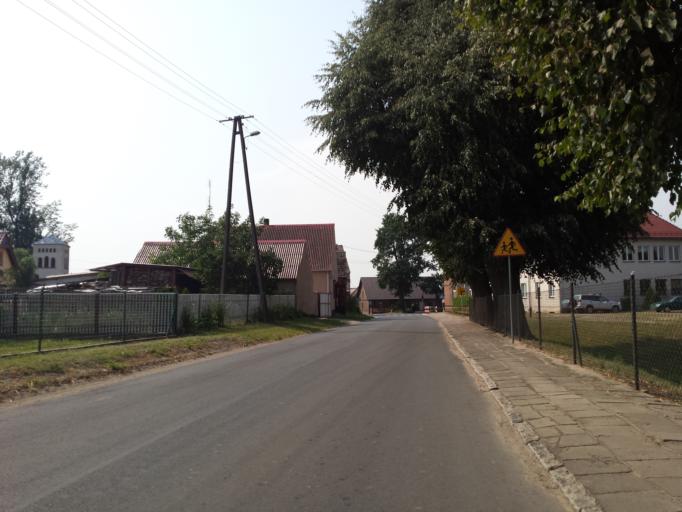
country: PL
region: Greater Poland Voivodeship
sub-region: Powiat czarnkowsko-trzcianecki
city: Polajewo
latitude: 52.7746
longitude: 16.6424
